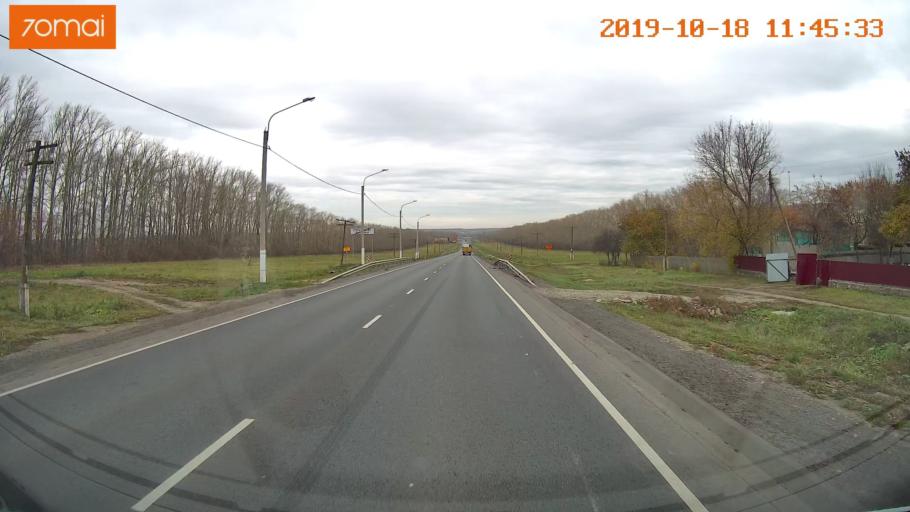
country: RU
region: Rjazan
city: Mikhaylov
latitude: 54.2115
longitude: 38.9715
